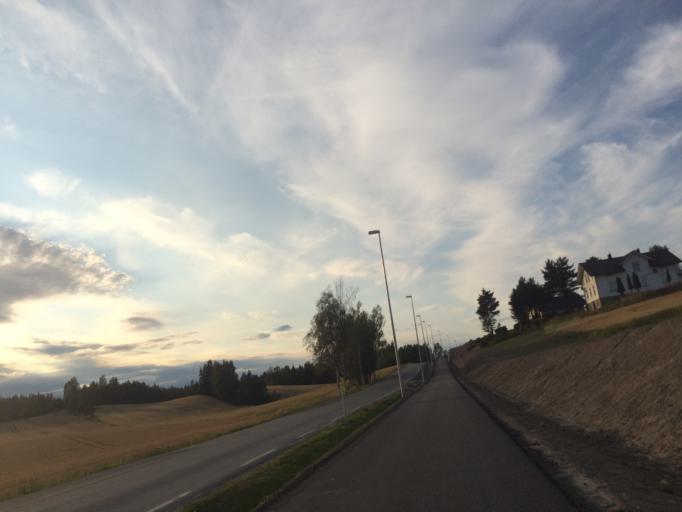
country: NO
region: Akershus
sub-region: Ski
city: Ski
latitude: 59.6913
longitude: 10.8624
